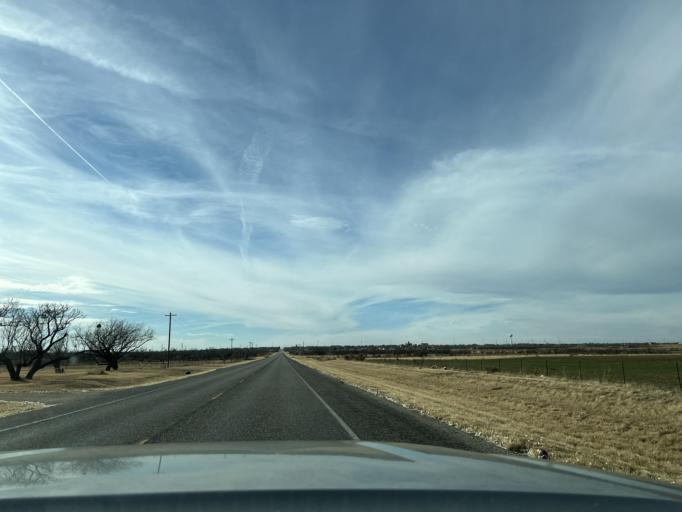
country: US
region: Texas
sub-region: Jones County
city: Anson
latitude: 32.7514
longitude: -99.8730
